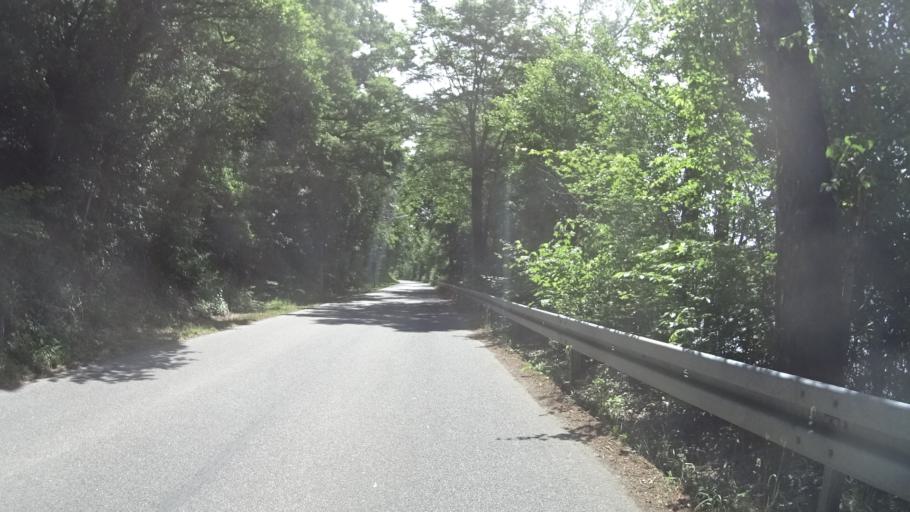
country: DE
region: Bavaria
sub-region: Lower Bavaria
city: Teugn
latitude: 48.9310
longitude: 12.0021
